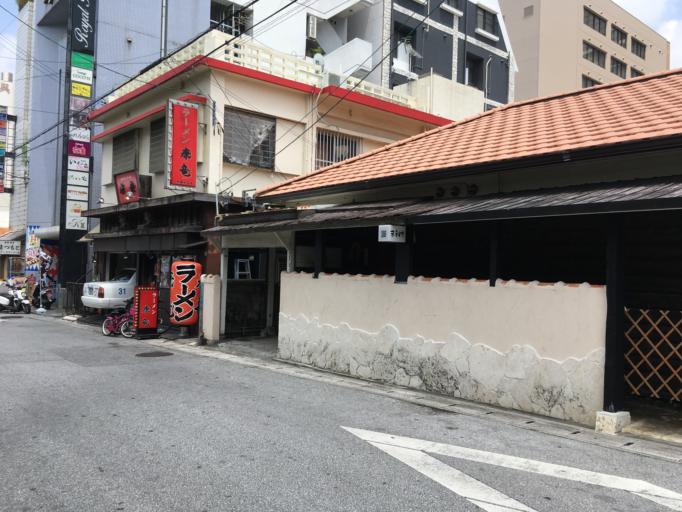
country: JP
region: Okinawa
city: Naha-shi
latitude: 26.2165
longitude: 127.6780
